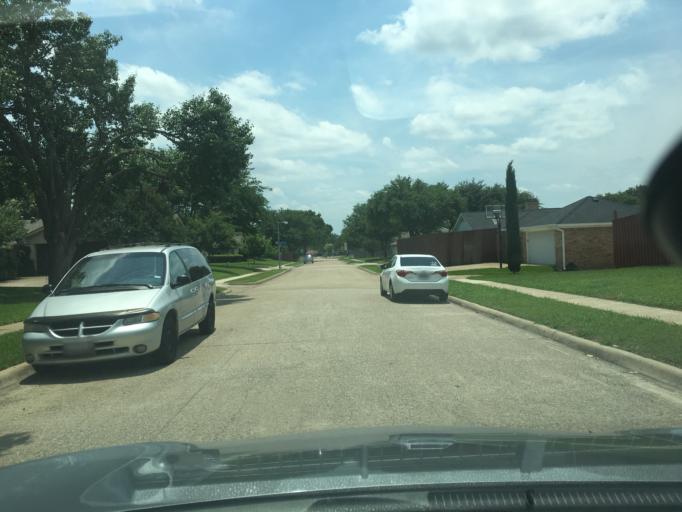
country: US
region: Texas
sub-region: Dallas County
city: Richardson
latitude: 32.9565
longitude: -96.6887
